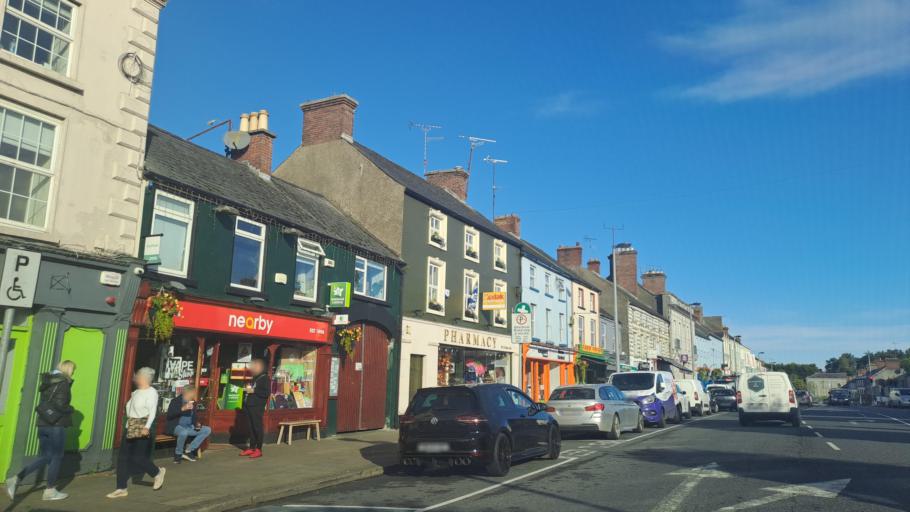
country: IE
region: Ulster
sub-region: County Monaghan
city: Carrickmacross
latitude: 53.9751
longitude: -6.7188
